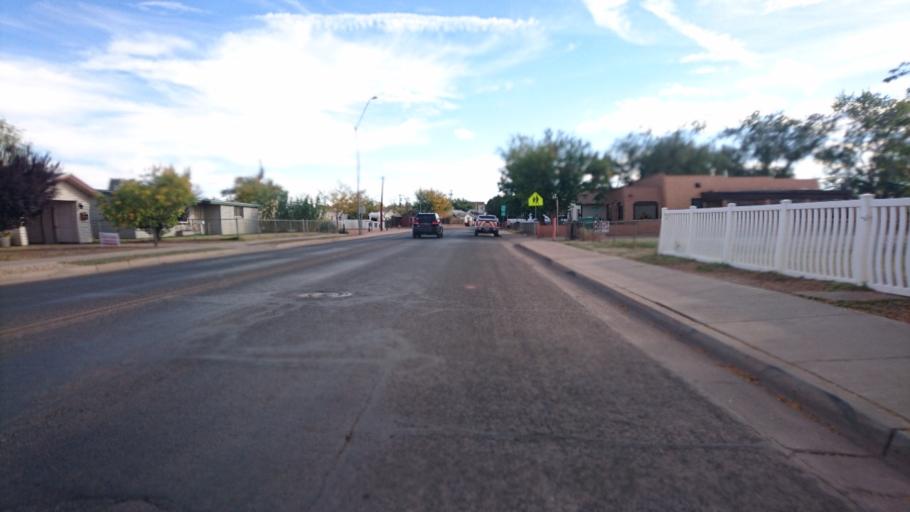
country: US
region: Arizona
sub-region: Navajo County
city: Winslow
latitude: 35.0318
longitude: -110.6978
